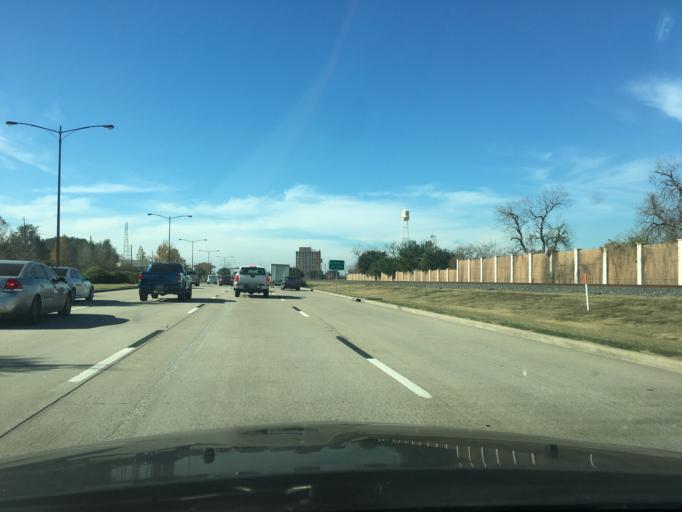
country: US
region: Texas
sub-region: Fort Bend County
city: Sugar Land
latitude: 29.6217
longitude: -95.6271
